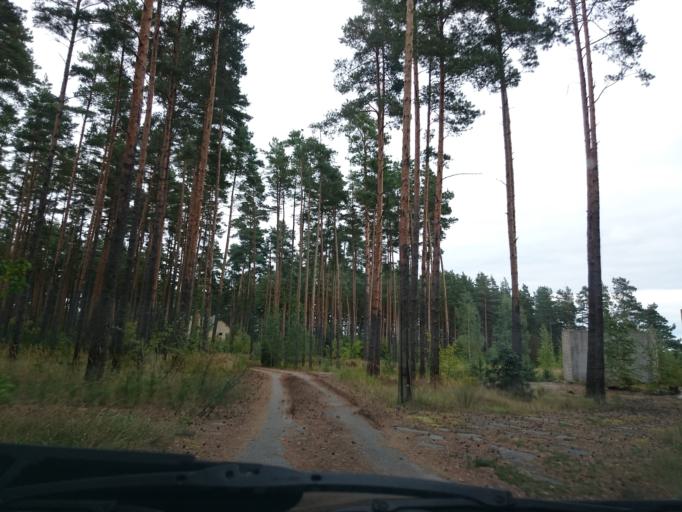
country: LV
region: Adazi
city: Adazi
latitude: 57.0534
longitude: 24.3230
